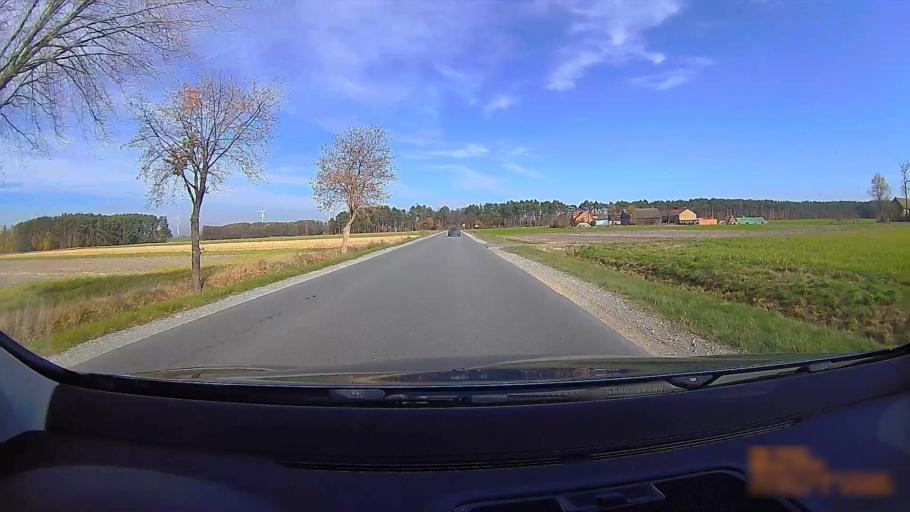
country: PL
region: Greater Poland Voivodeship
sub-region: Powiat ostrzeszowski
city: Doruchow
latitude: 51.3821
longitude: 18.0448
